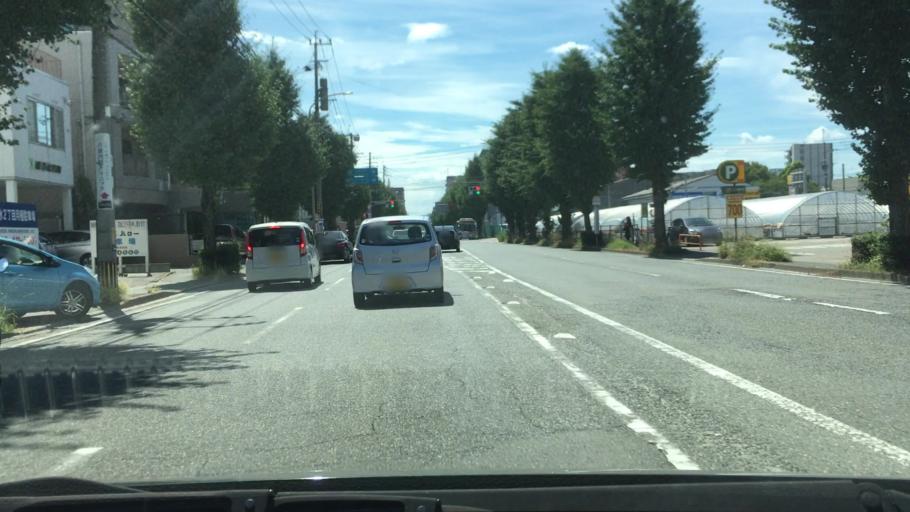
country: JP
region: Fukuoka
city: Fukuoka-shi
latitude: 33.5726
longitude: 130.4222
